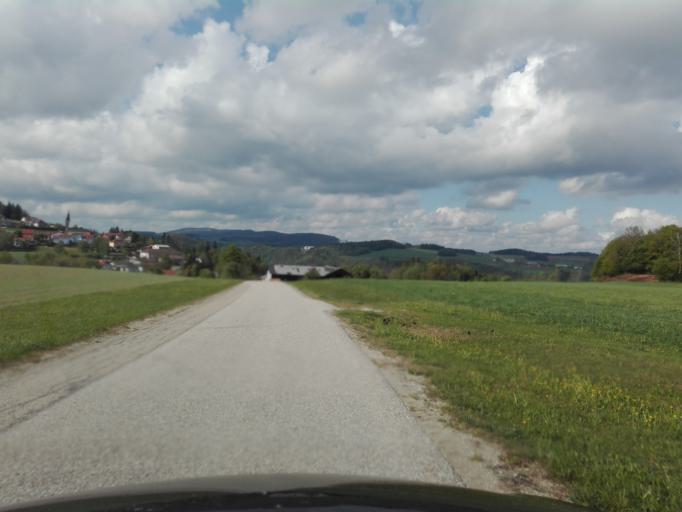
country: AT
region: Upper Austria
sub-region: Politischer Bezirk Rohrbach
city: Pfarrkirchen im Muehlkreis
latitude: 48.4334
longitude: 13.8253
